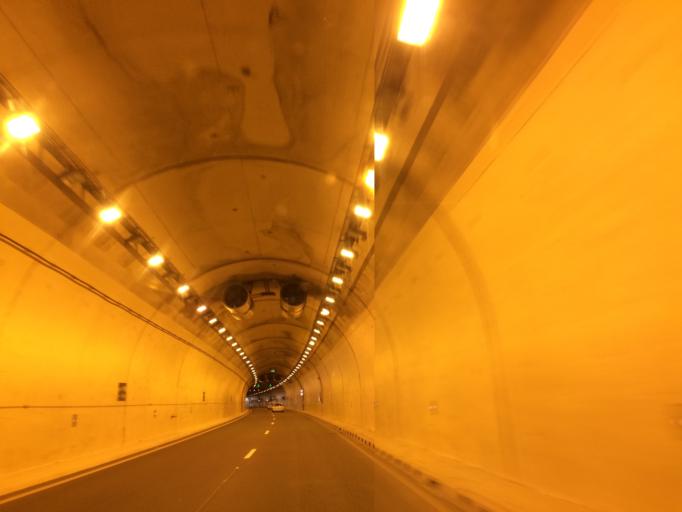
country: MA
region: Marrakech-Tensift-Al Haouz
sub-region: Chichaoua
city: Taouloukoult
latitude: 31.1914
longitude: -8.9814
